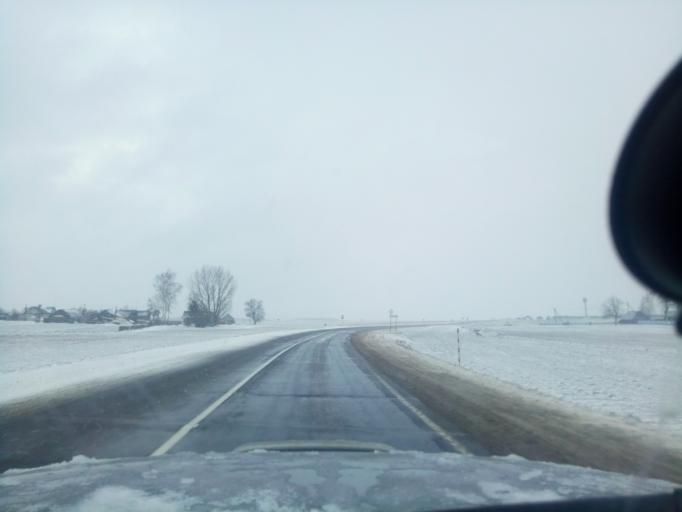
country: BY
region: Minsk
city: Haradzyeya
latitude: 53.3023
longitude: 26.5748
